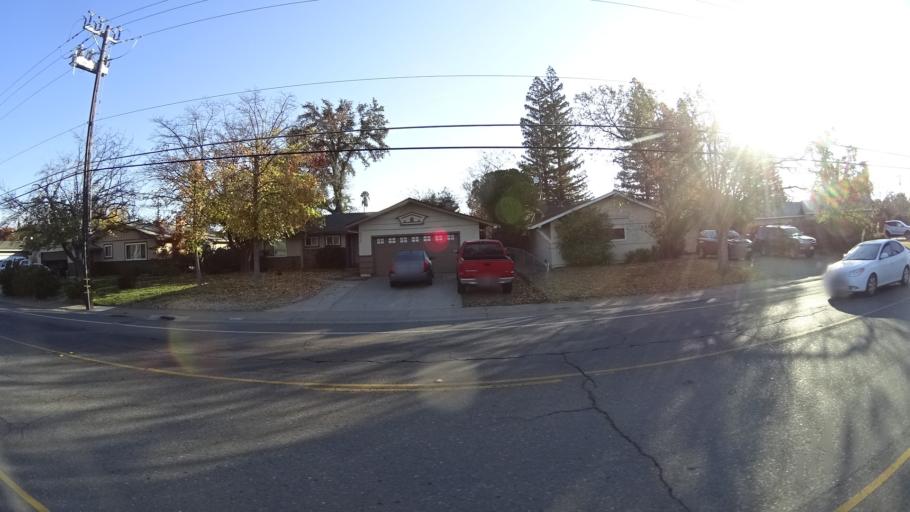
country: US
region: California
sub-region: Sacramento County
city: Antelope
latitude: 38.6894
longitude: -121.3088
